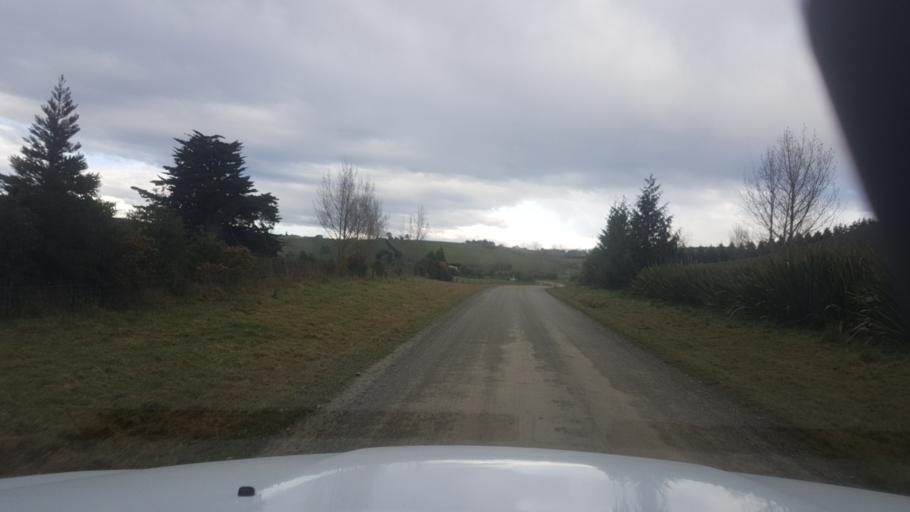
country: NZ
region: Canterbury
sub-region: Timaru District
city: Pleasant Point
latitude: -44.3412
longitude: 171.1641
